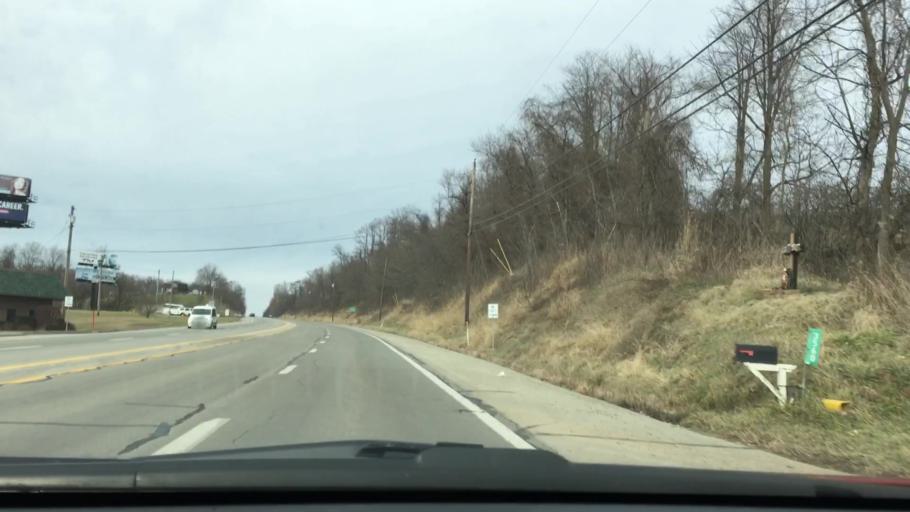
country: US
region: Pennsylvania
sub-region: Fayette County
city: Perryopolis
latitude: 40.0971
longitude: -79.7631
